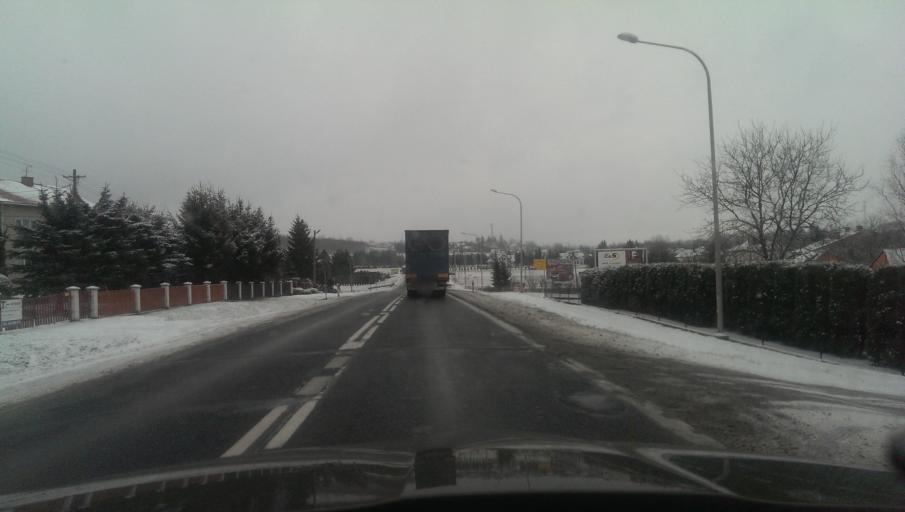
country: PL
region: Subcarpathian Voivodeship
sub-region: Powiat sanocki
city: Dlugie
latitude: 49.5761
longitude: 22.0503
